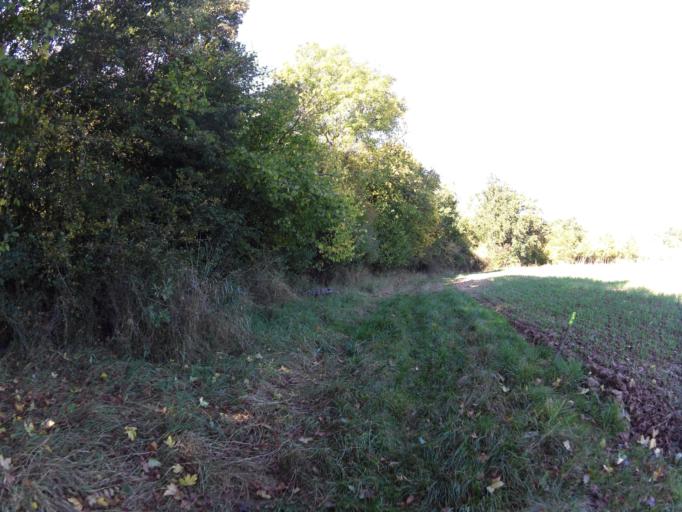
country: DE
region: Bavaria
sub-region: Regierungsbezirk Unterfranken
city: Ochsenfurt
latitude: 49.6881
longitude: 10.0532
